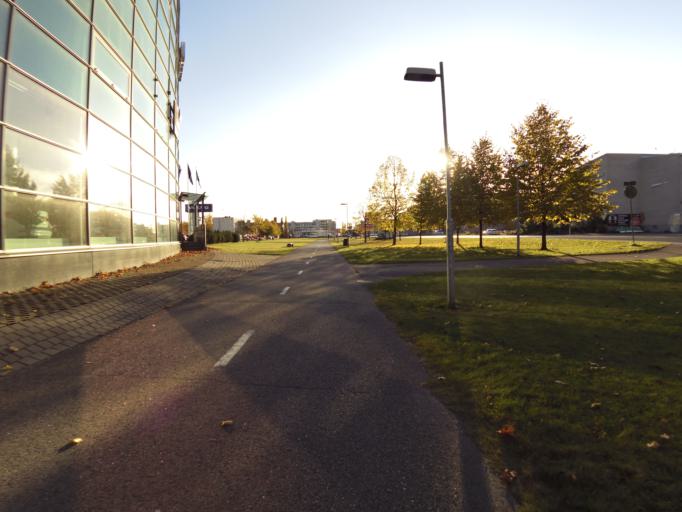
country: FI
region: Uusimaa
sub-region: Helsinki
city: Vantaa
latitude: 60.1958
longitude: 25.0387
